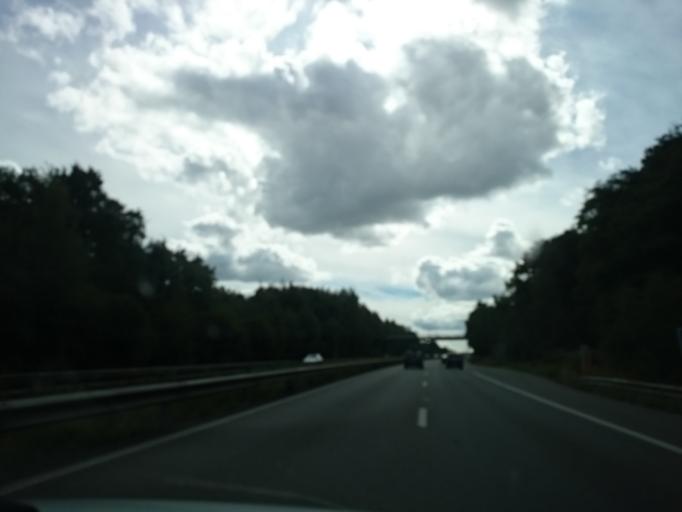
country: FR
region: Pays de la Loire
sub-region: Departement de la Loire-Atlantique
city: Les Sorinieres
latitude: 47.1645
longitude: -1.5246
